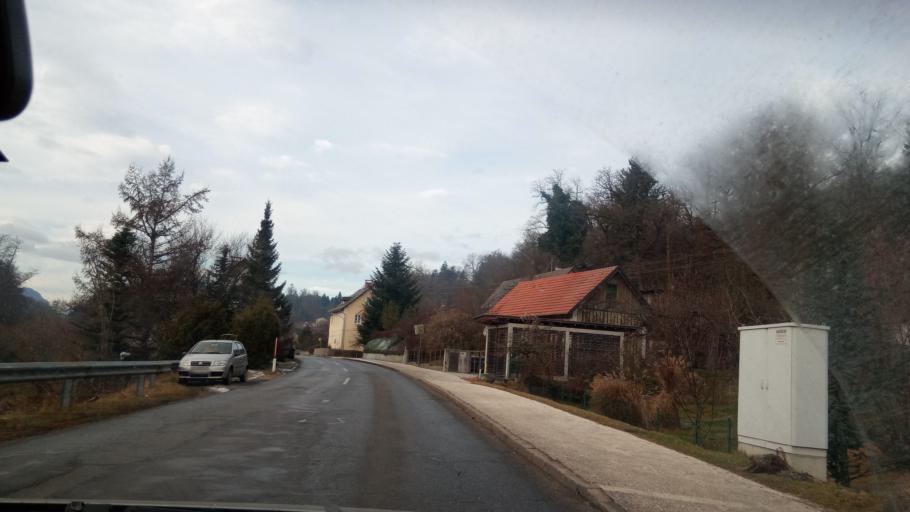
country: AT
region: Carinthia
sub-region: Politischer Bezirk Klagenfurt Land
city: Kottmannsdorf
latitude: 46.5901
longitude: 14.2578
